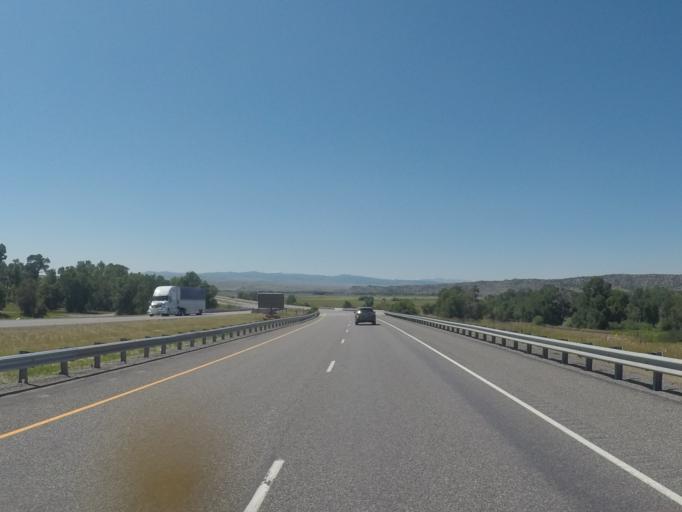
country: US
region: Montana
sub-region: Park County
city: Livingston
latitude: 45.7128
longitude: -110.3965
